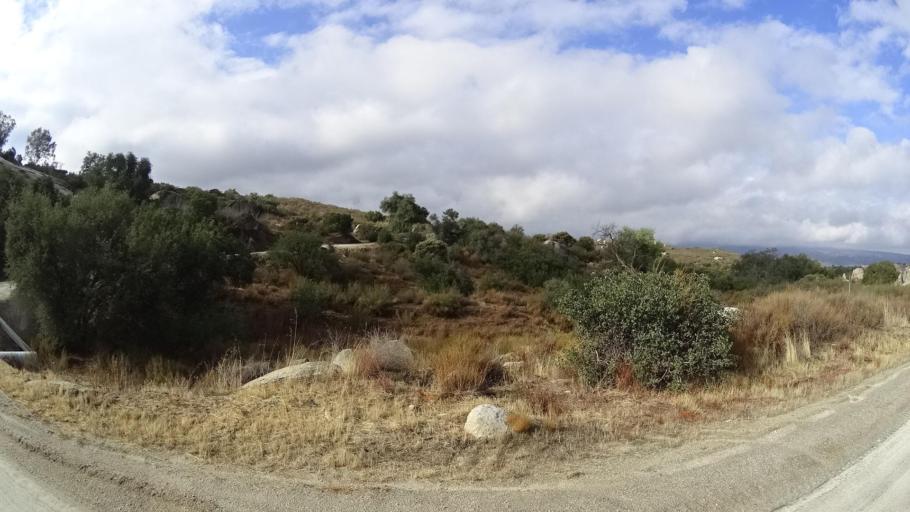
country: MX
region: Baja California
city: Tecate
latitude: 32.6426
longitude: -116.6350
